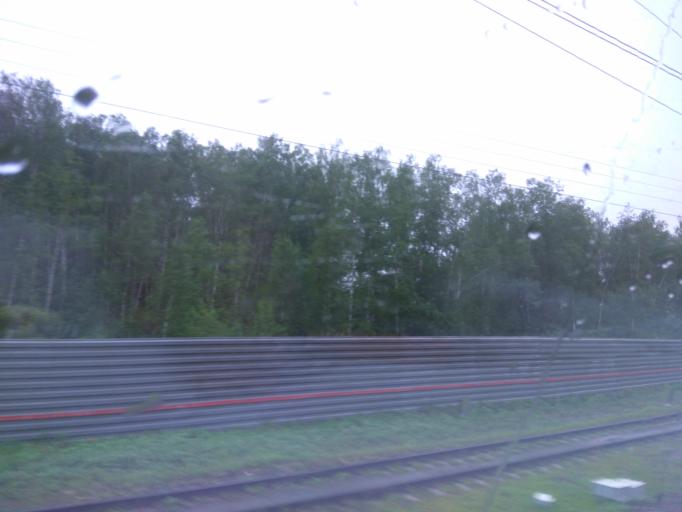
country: RU
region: Moskovskaya
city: Stupino
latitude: 54.9154
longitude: 38.0729
